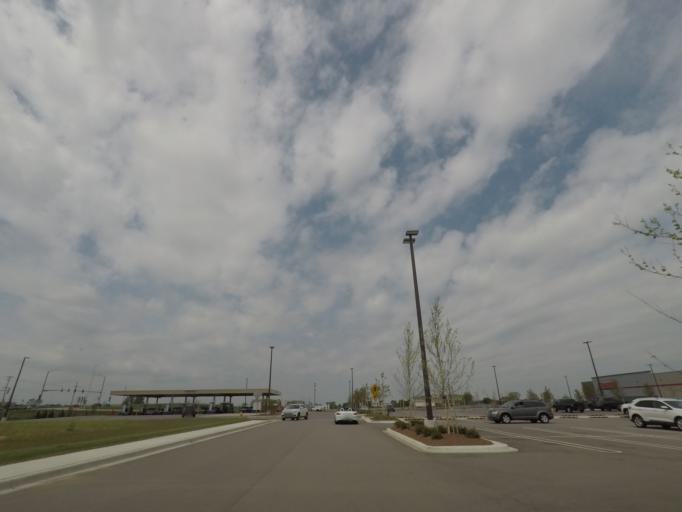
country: US
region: Illinois
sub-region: Winnebago County
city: Machesney Park
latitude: 42.3201
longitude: -88.9608
